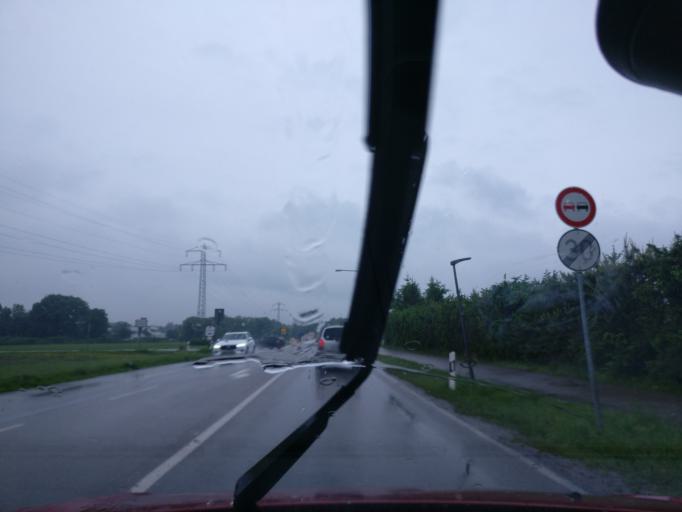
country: DE
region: Bavaria
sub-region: Upper Bavaria
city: Dachau
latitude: 48.2485
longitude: 11.4549
